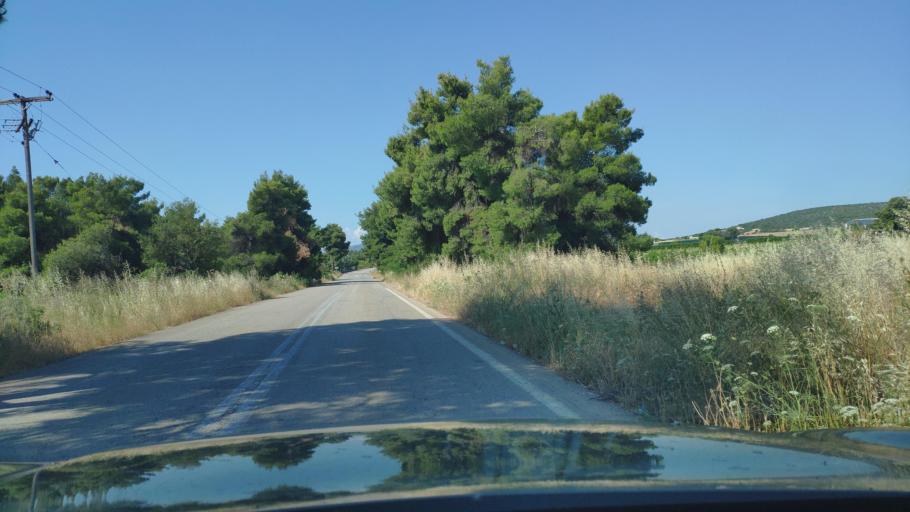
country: GR
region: Central Greece
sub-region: Nomos Voiotias
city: Arma
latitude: 38.3948
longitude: 23.5102
